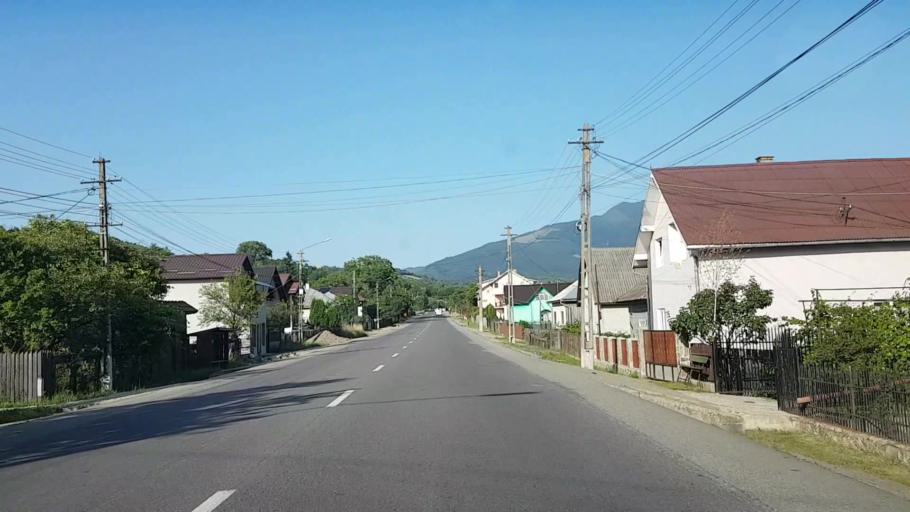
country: RO
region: Bistrita-Nasaud
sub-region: Comuna Tiha Bargaului
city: Tiha Bargaului
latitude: 47.2277
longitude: 24.7716
